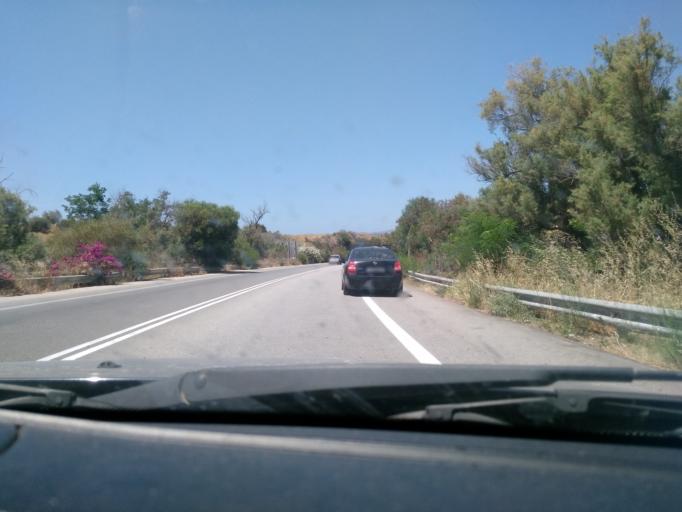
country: GR
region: Crete
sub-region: Nomos Chanias
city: Kalivai
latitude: 35.4316
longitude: 24.1661
